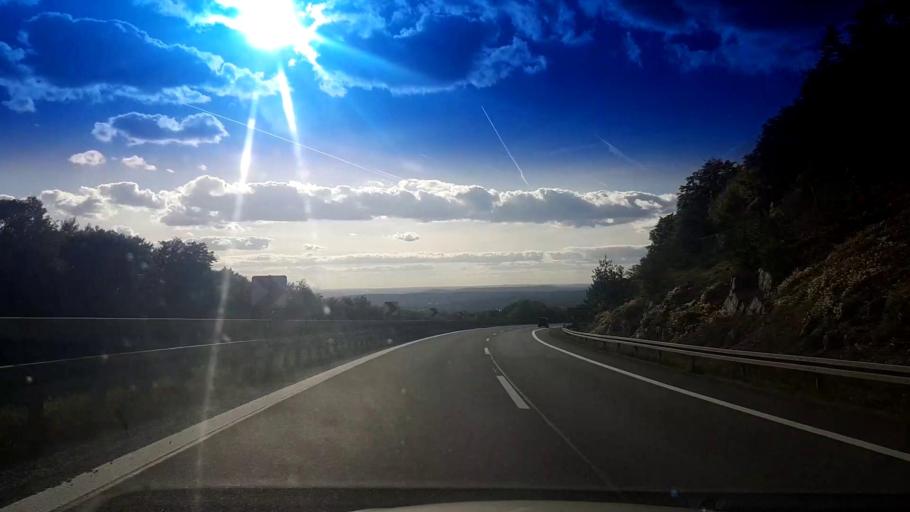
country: DE
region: Bavaria
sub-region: Upper Franconia
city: Schesslitz
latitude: 49.9870
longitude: 11.0889
